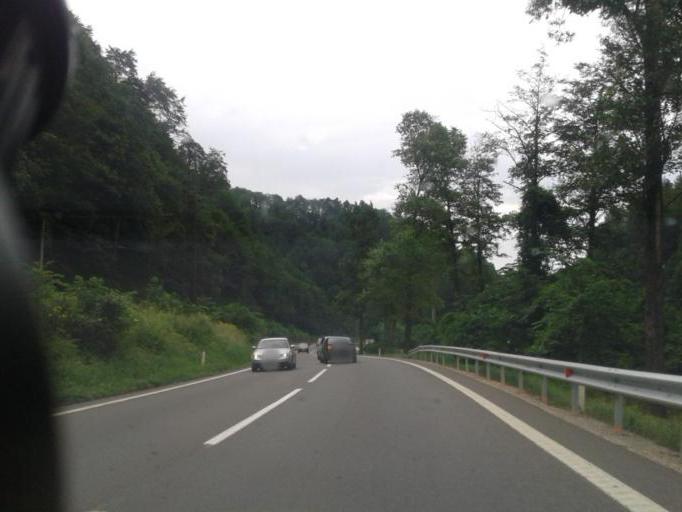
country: RO
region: Brasov
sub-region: Oras Predeal
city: Predeal
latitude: 45.5678
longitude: 25.6081
